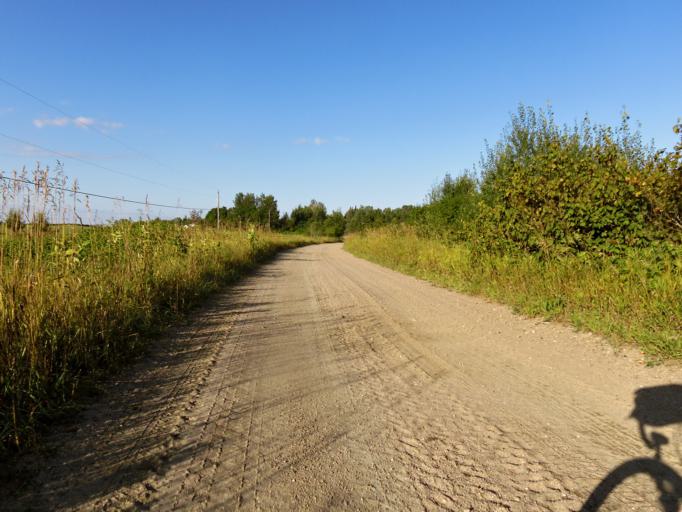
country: CA
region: Quebec
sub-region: Outaouais
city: Maniwaki
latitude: 46.3029
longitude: -76.0194
